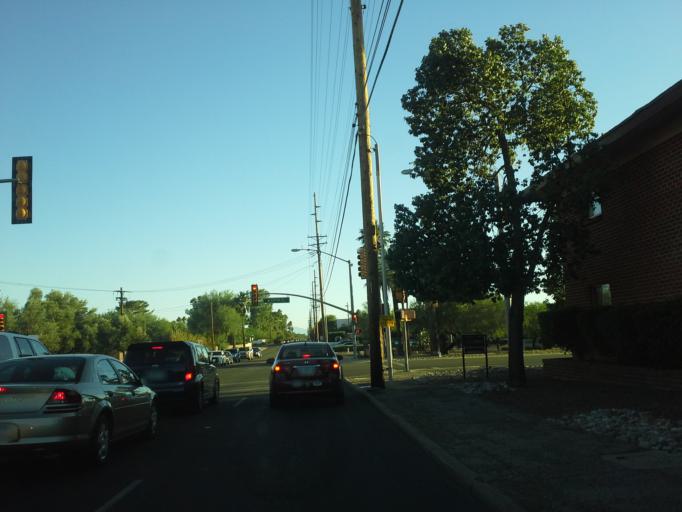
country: US
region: Arizona
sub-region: Pima County
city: Tucson
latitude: 32.2290
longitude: -110.9268
